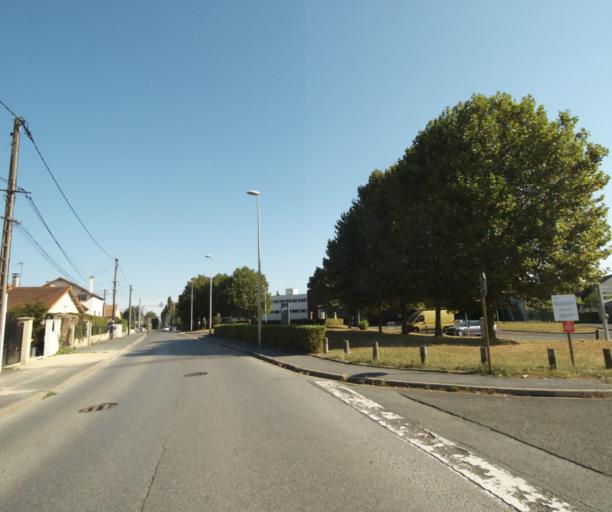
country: FR
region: Ile-de-France
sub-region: Departement de Seine-et-Marne
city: Lagny-sur-Marne
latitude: 48.8667
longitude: 2.7194
